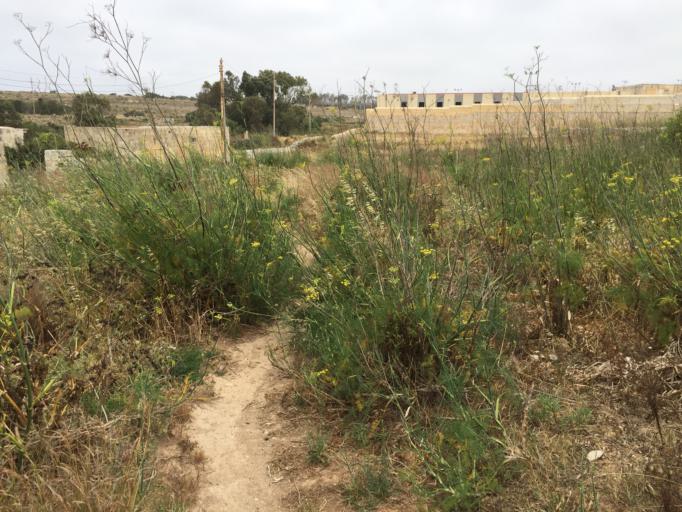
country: MT
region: Dingli
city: Dingli
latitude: 35.8810
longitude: 14.3557
